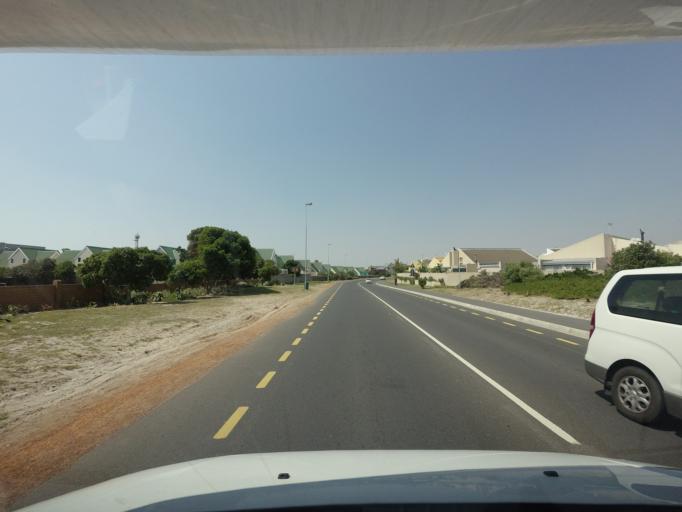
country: ZA
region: Western Cape
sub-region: City of Cape Town
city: Sunset Beach
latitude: -33.7282
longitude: 18.4449
